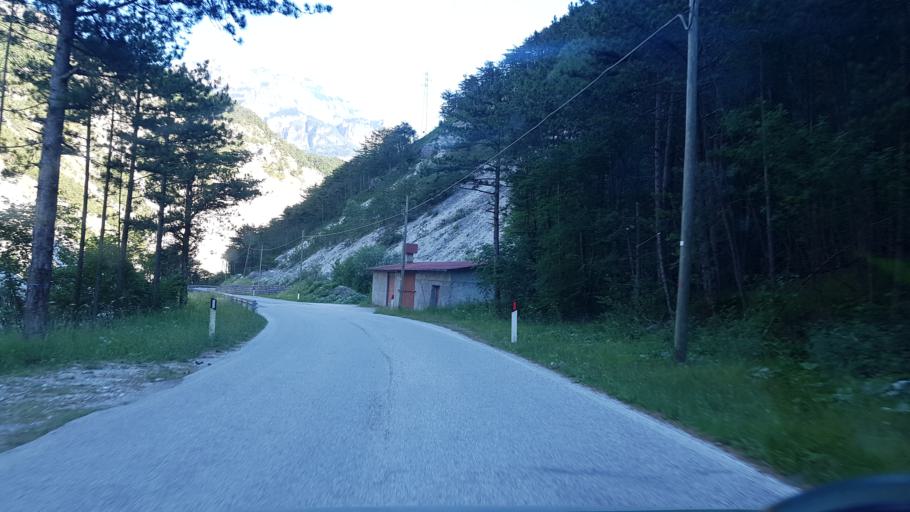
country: IT
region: Friuli Venezia Giulia
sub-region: Provincia di Udine
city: Moggio Udinese
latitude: 46.4445
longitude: 13.1909
